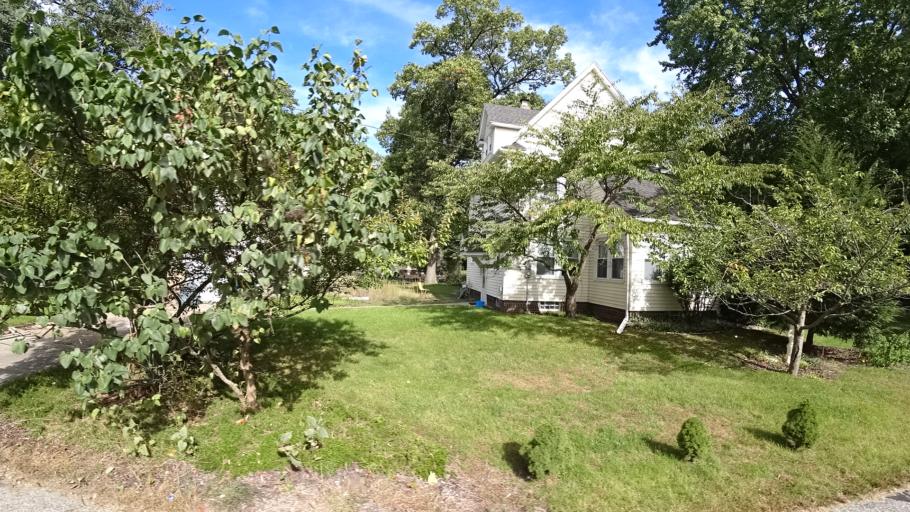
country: US
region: Indiana
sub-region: LaPorte County
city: Michigan City
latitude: 41.7205
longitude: -86.8740
